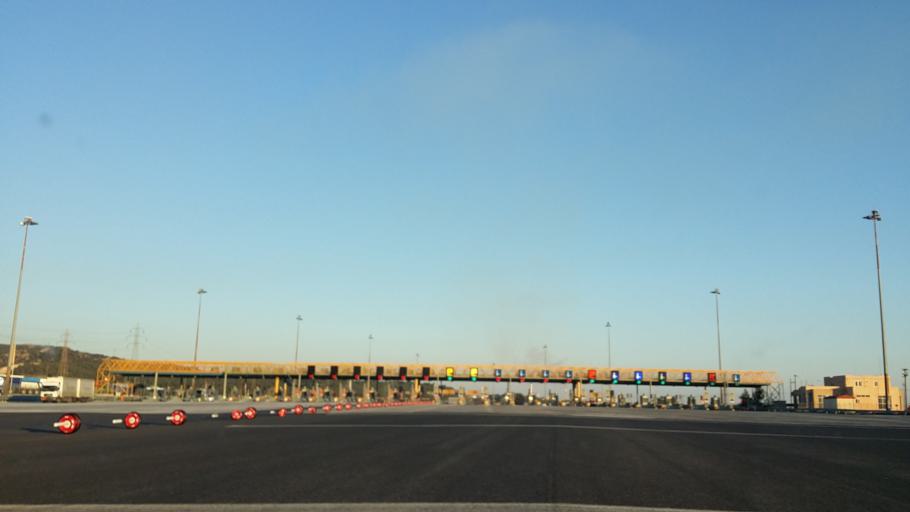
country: GR
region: Peloponnese
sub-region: Nomos Korinthias
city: Isthmia
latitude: 37.9253
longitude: 23.0300
